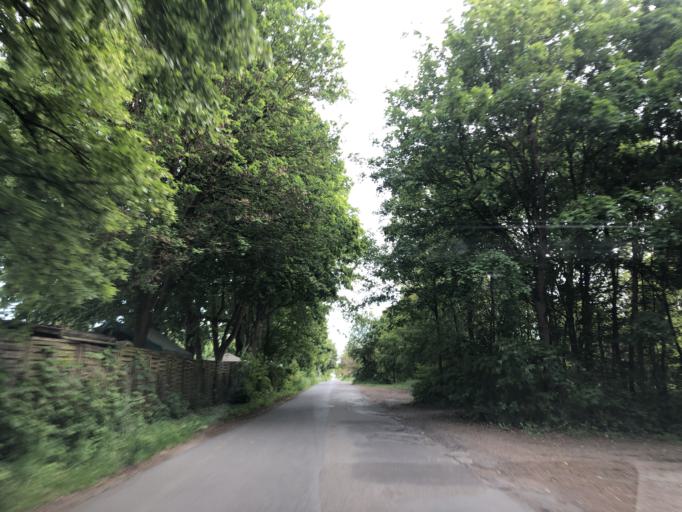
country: DE
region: Hesse
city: Weiterstadt
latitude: 49.9443
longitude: 8.6037
